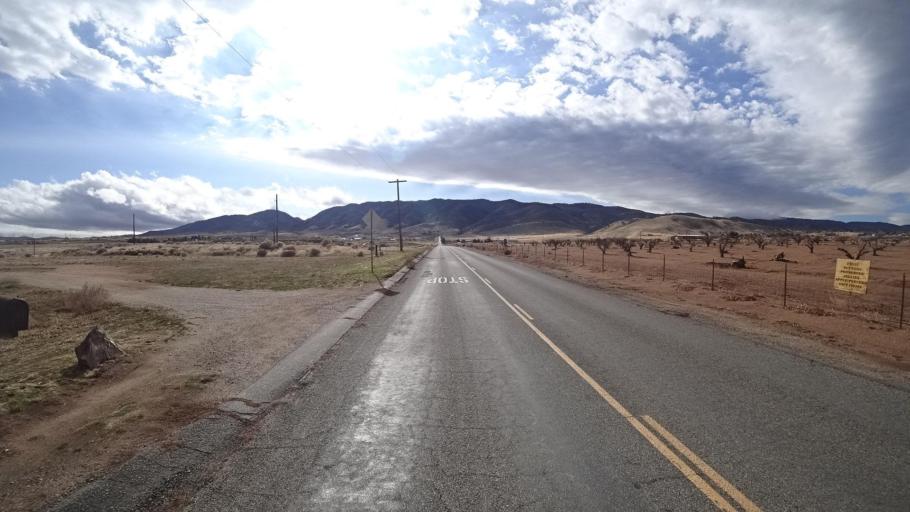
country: US
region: California
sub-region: Kern County
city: Tehachapi
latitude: 35.1192
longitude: -118.4678
